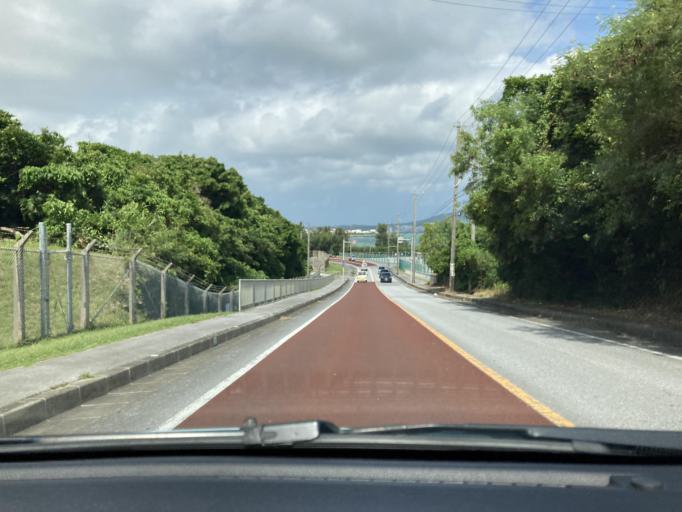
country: JP
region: Okinawa
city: Ishikawa
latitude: 26.4036
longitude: 127.8448
